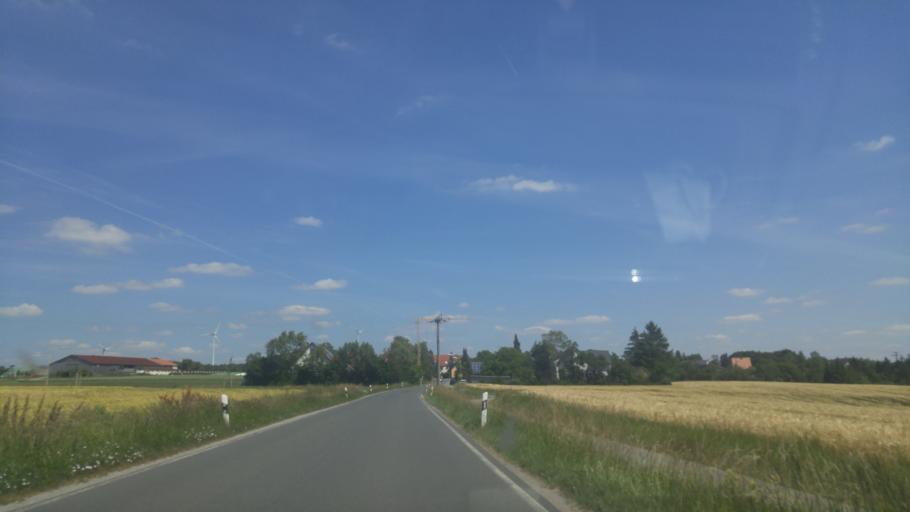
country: DE
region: Bavaria
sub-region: Regierungsbezirk Mittelfranken
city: Hagenbuchach
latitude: 49.5357
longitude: 10.7857
